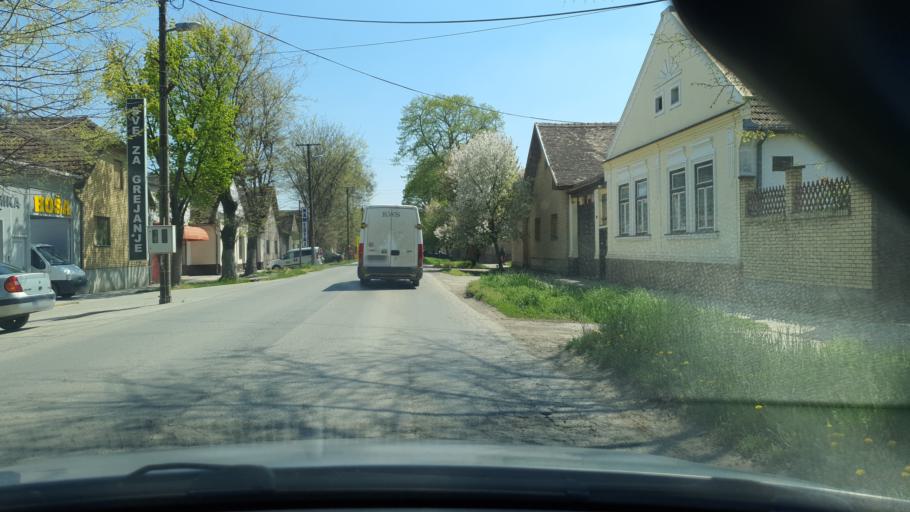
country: RS
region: Autonomna Pokrajina Vojvodina
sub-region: Zapadnobacki Okrug
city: Odzaci
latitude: 45.5097
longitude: 19.2547
